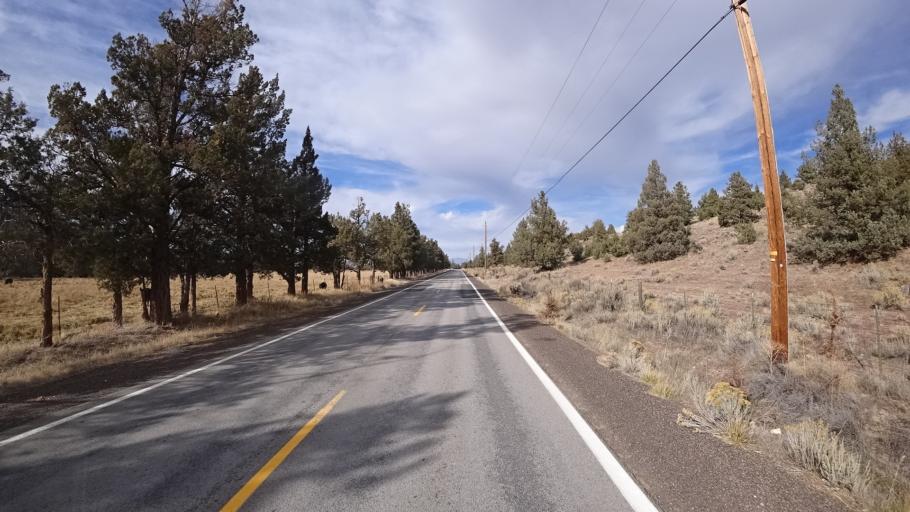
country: US
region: California
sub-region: Siskiyou County
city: Weed
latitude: 41.5773
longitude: -122.3961
